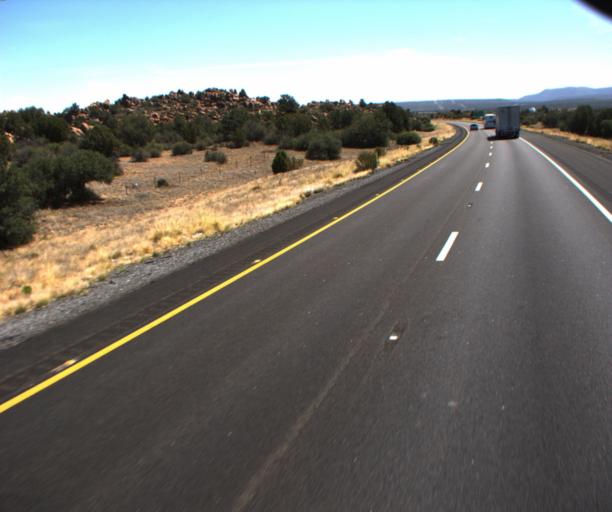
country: US
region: Arizona
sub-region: Mohave County
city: Peach Springs
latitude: 35.1836
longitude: -113.3881
